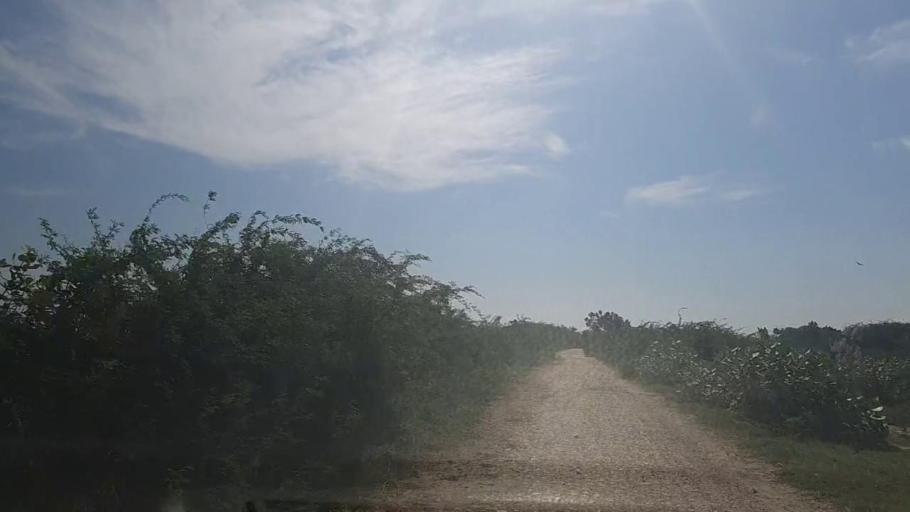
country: PK
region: Sindh
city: Mirpur Batoro
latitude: 24.6809
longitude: 68.1816
